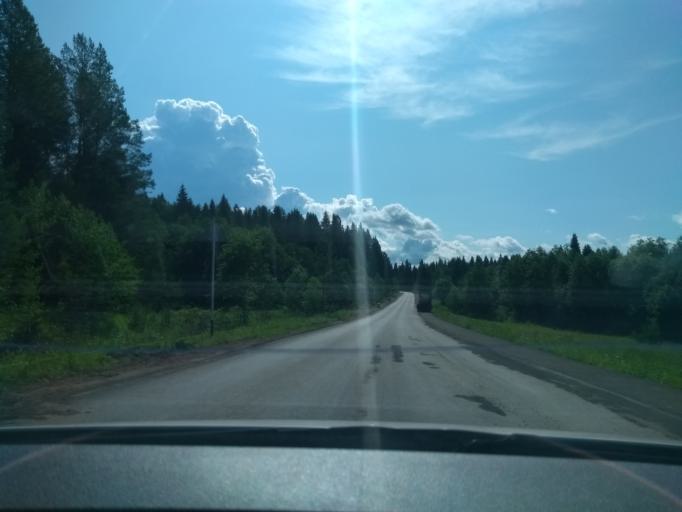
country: RU
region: Perm
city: Bershet'
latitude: 57.8198
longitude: 56.5245
